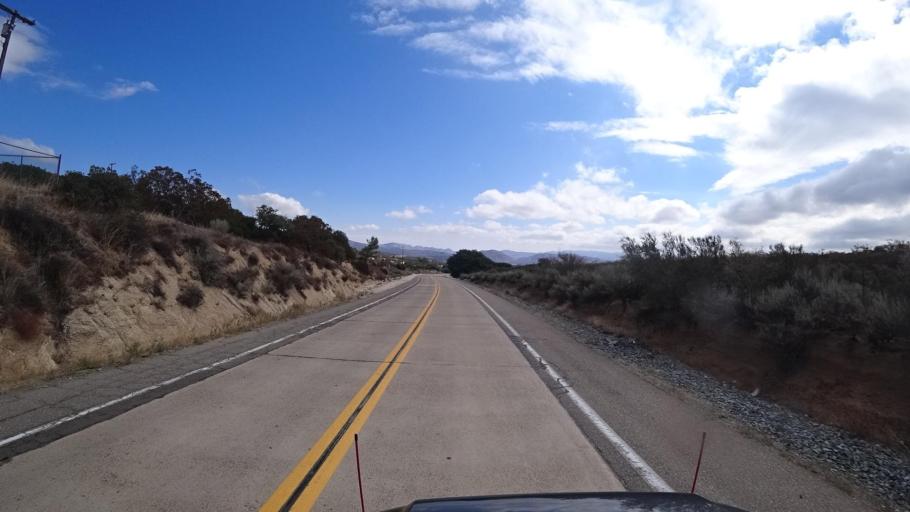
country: US
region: California
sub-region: San Diego County
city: Campo
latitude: 32.6693
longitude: -116.3116
